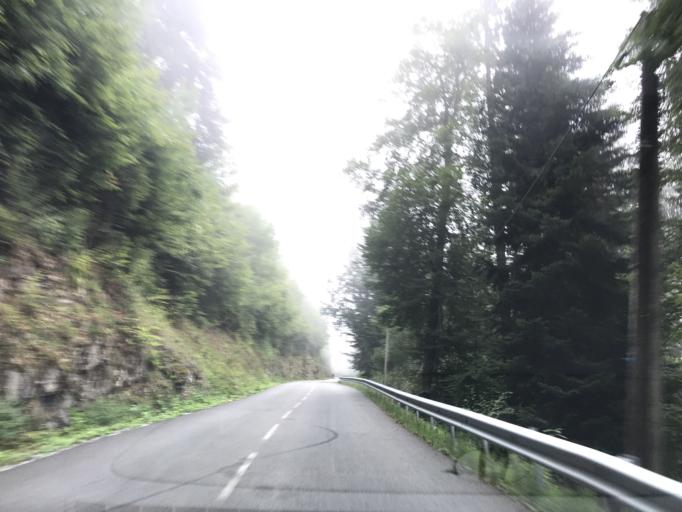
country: FR
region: Rhone-Alpes
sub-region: Departement de la Haute-Savoie
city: Talloires
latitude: 45.8159
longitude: 6.2437
